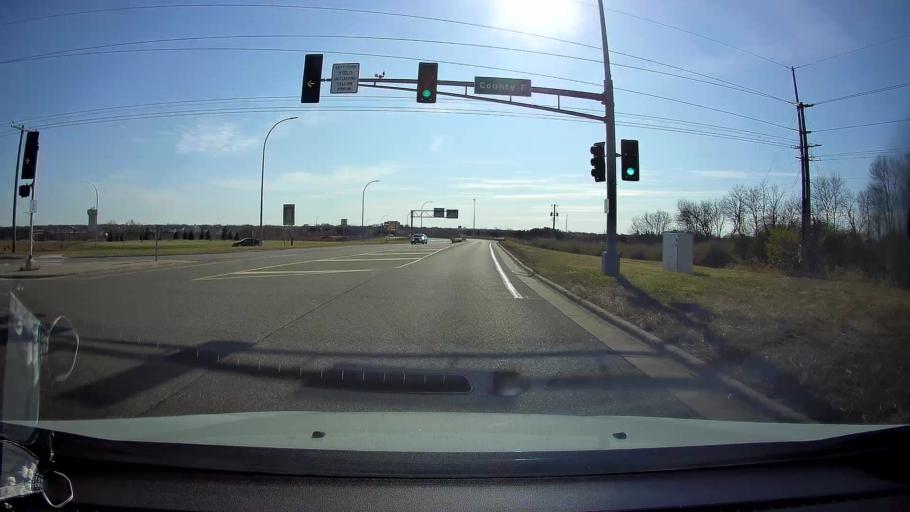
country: US
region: Minnesota
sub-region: Ramsey County
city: Arden Hills
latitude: 45.0649
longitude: -93.1576
